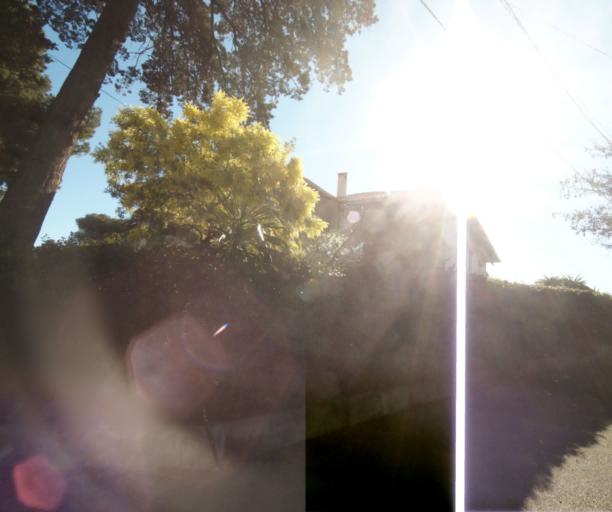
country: FR
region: Provence-Alpes-Cote d'Azur
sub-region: Departement des Alpes-Maritimes
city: Antibes
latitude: 43.5716
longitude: 7.1198
